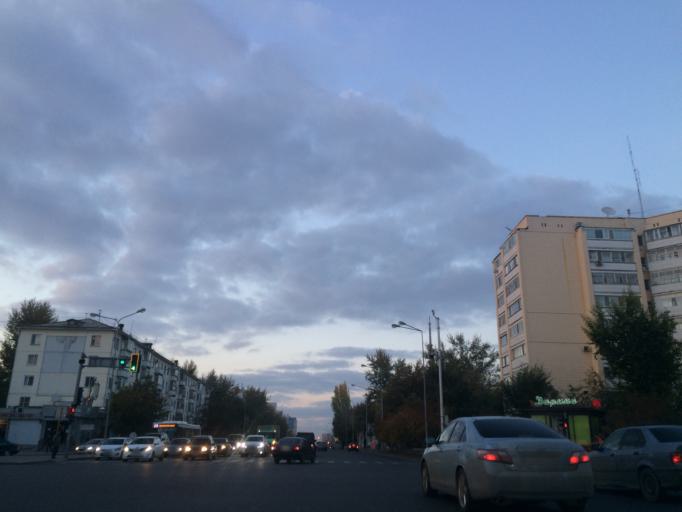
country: KZ
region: Astana Qalasy
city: Astana
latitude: 51.1756
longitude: 71.4112
